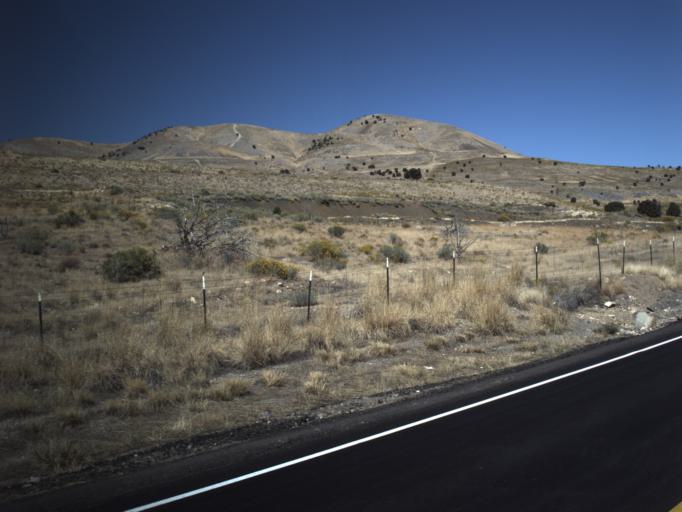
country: US
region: Utah
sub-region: Utah County
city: Saratoga Springs
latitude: 40.2195
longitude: -111.8818
